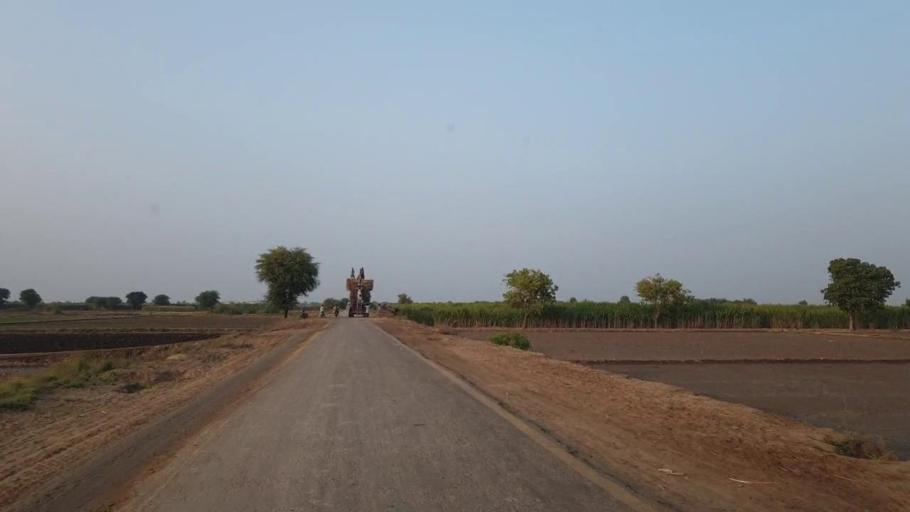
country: PK
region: Sindh
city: Tando Ghulam Ali
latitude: 25.1316
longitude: 68.9587
